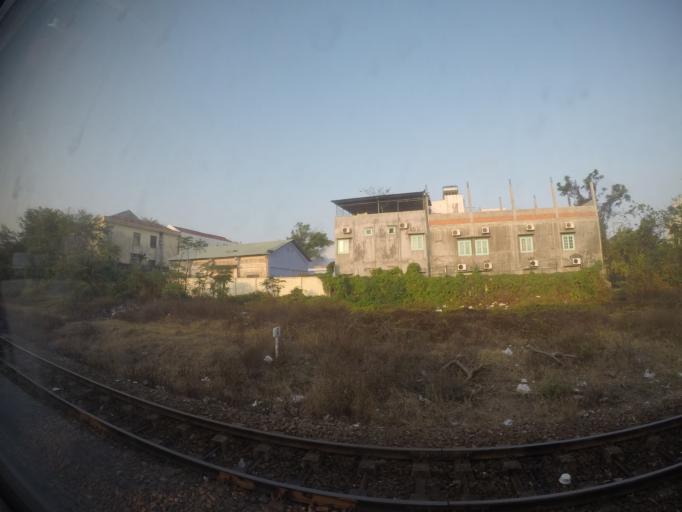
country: VN
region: Phu Yen
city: Tuy Hoa
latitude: 13.0879
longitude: 109.2969
